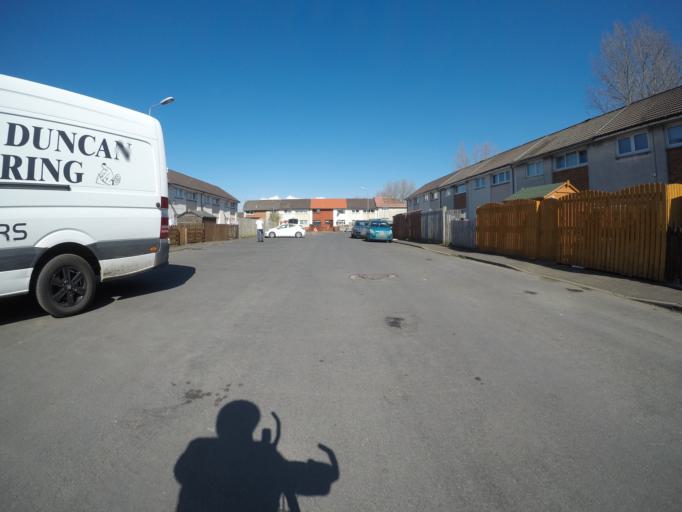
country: GB
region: Scotland
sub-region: North Ayrshire
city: Irvine
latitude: 55.6309
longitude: -4.6587
